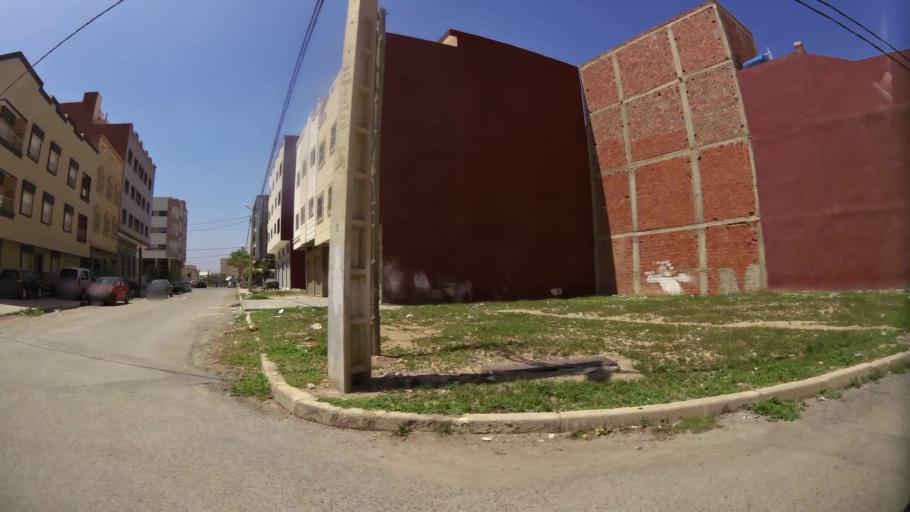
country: MA
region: Oriental
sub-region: Oujda-Angad
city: Oujda
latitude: 34.7006
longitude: -1.8896
